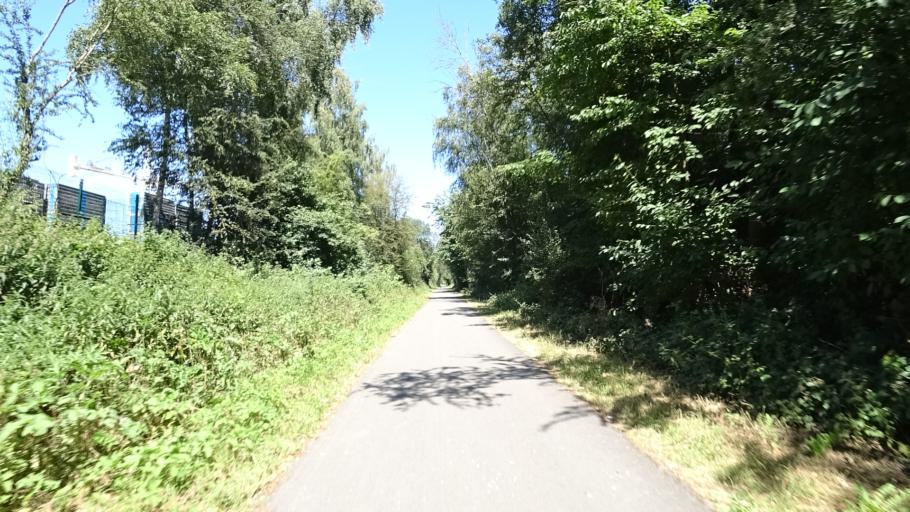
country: BE
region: Wallonia
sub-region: Province de Namur
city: Gembloux
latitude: 50.5785
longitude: 4.7096
